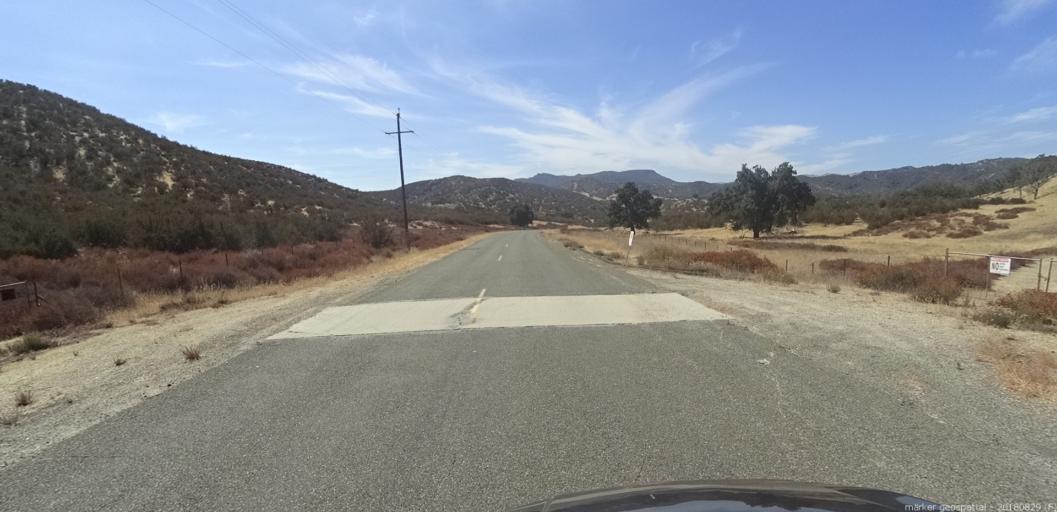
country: US
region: California
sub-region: San Luis Obispo County
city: Lake Nacimiento
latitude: 35.8200
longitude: -120.9799
